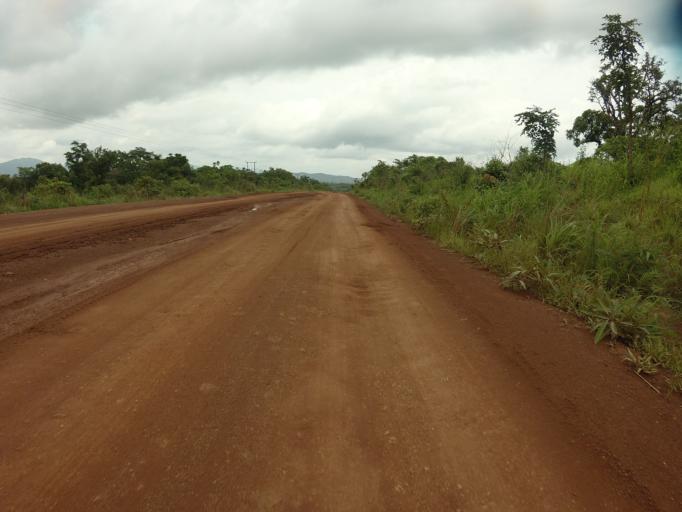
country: GH
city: Kpandae
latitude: 8.3049
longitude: 0.4850
